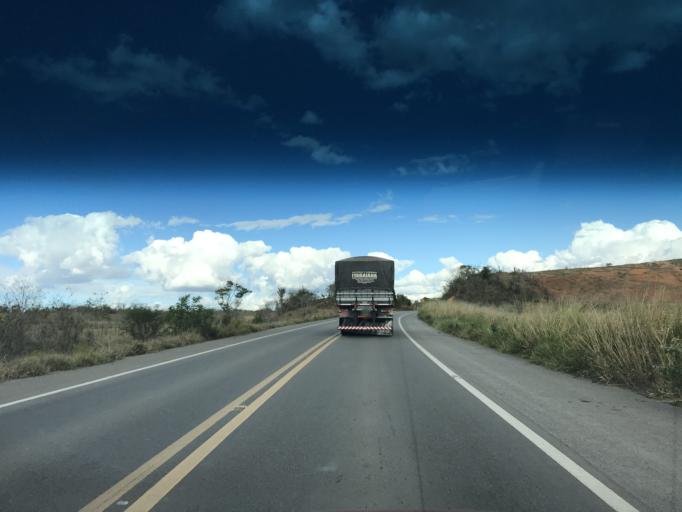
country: BR
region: Bahia
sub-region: Ruy Barbosa
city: Terra Nova
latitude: -12.4397
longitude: -40.8124
